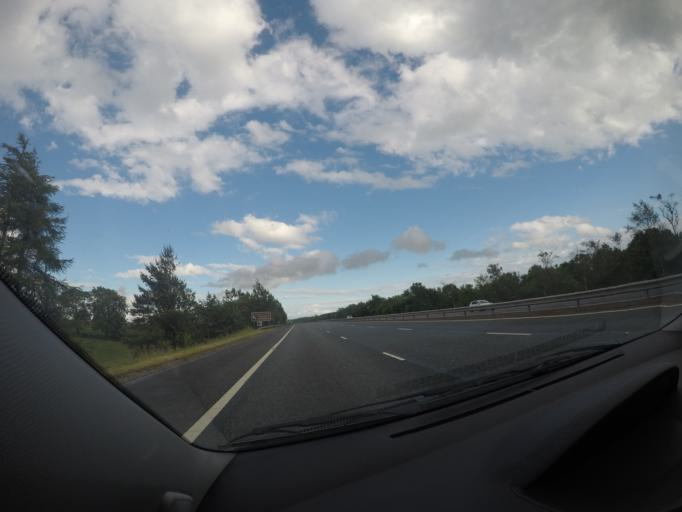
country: GB
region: Scotland
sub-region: Dumfries and Galloway
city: Annan
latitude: 55.0683
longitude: -3.2853
